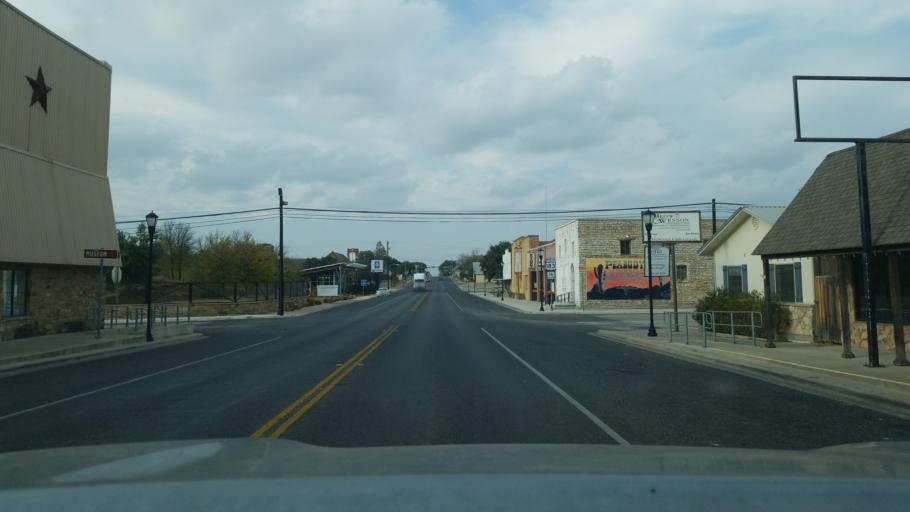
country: US
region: Texas
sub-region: Mills County
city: Goldthwaite
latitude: 31.4512
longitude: -98.5695
